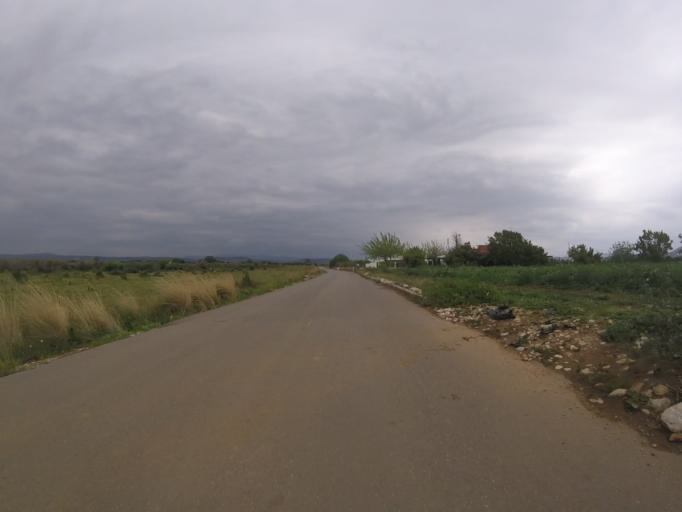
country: ES
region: Valencia
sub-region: Provincia de Castello
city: Torreblanca
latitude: 40.2126
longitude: 0.2485
